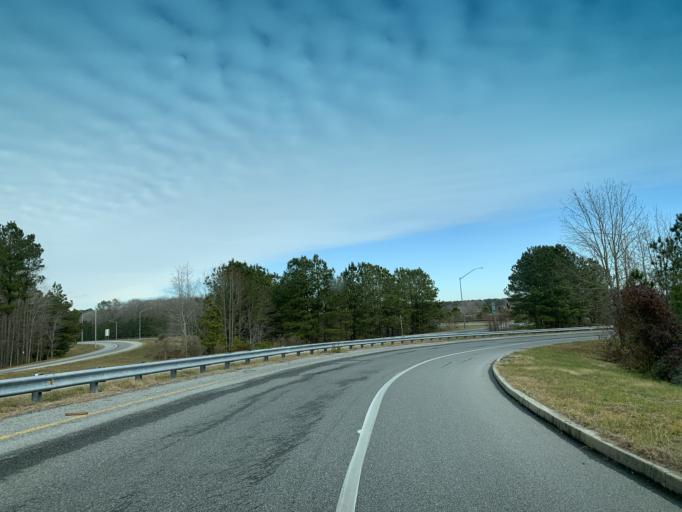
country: US
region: Maryland
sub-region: Worcester County
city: Ocean Pines
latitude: 38.3784
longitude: -75.2081
